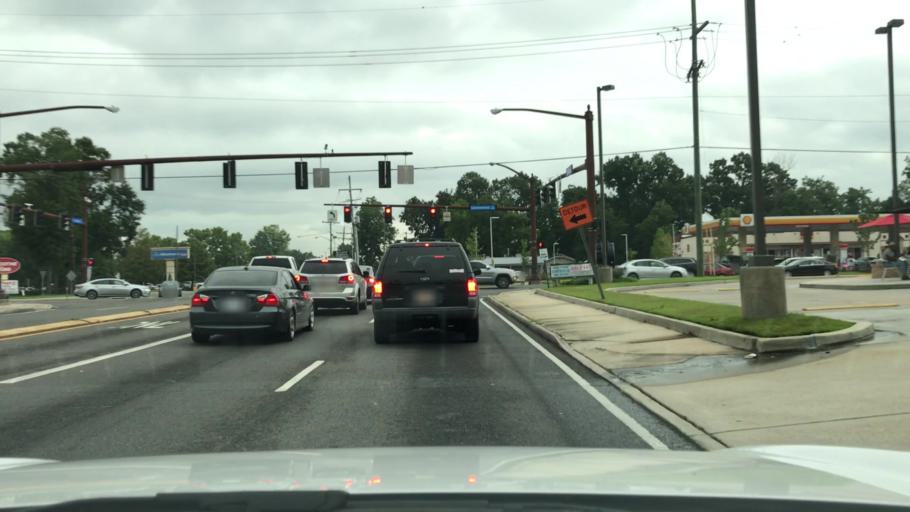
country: US
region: Louisiana
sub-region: East Baton Rouge Parish
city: Baton Rouge
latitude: 30.4440
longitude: -91.1384
